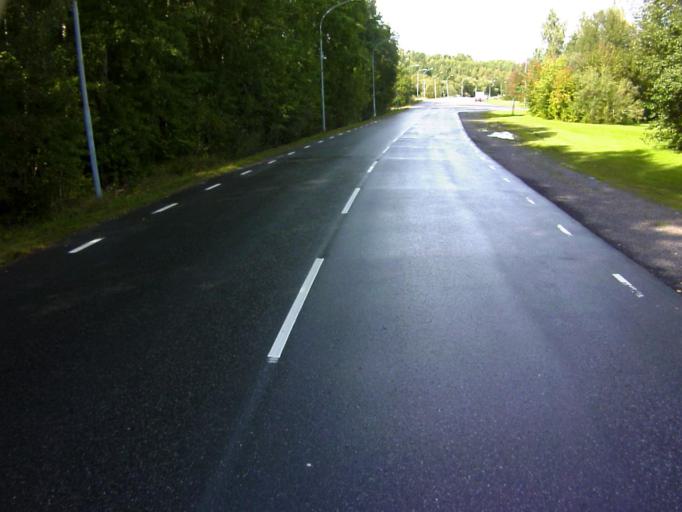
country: SE
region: Soedermanland
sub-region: Eskilstuna Kommun
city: Eskilstuna
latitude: 59.3908
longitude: 16.5306
